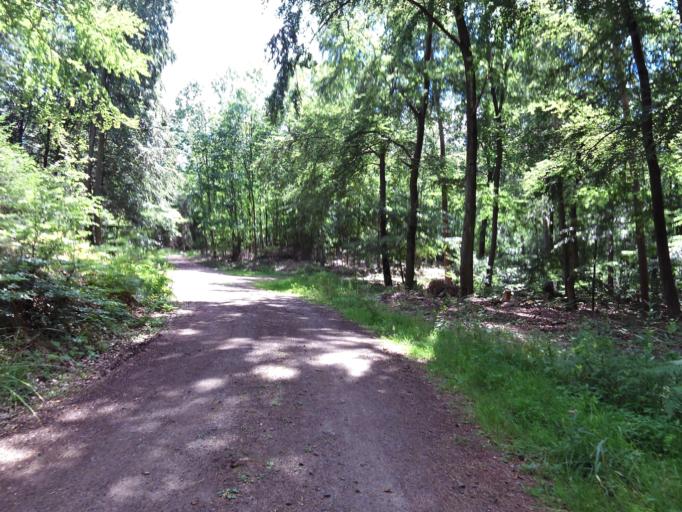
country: DE
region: Rheinland-Pfalz
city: Altleiningen
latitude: 49.4697
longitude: 8.0648
